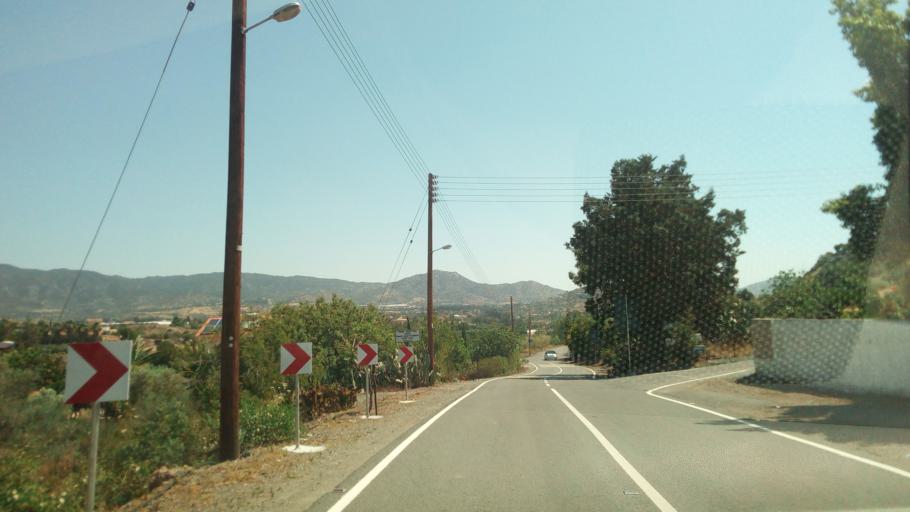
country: CY
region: Limassol
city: Parekklisha
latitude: 34.7452
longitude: 33.1632
